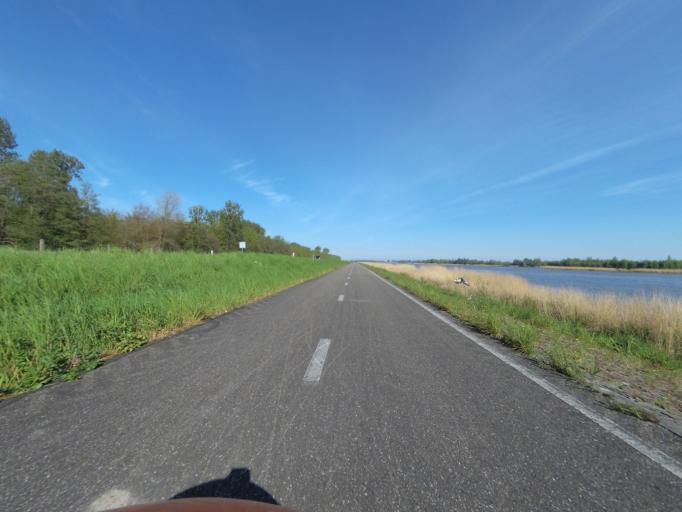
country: NL
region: Flevoland
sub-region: Gemeente Noordoostpolder
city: Ens
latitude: 52.5695
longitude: 5.8247
